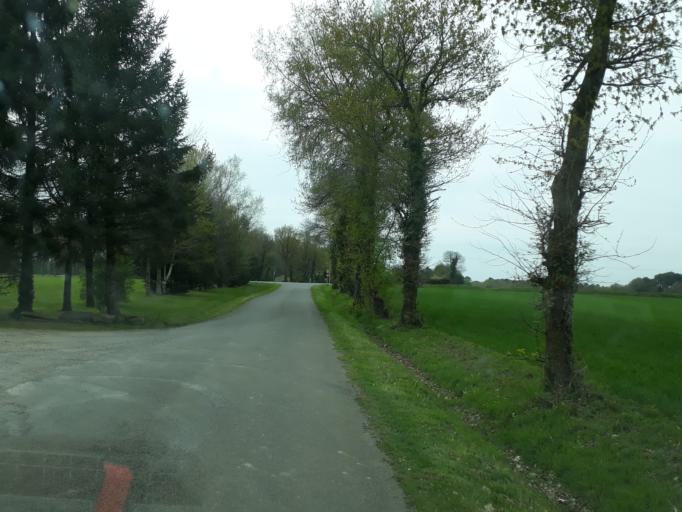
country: FR
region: Brittany
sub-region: Departement du Morbihan
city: Sulniac
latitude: 47.6779
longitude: -2.5891
